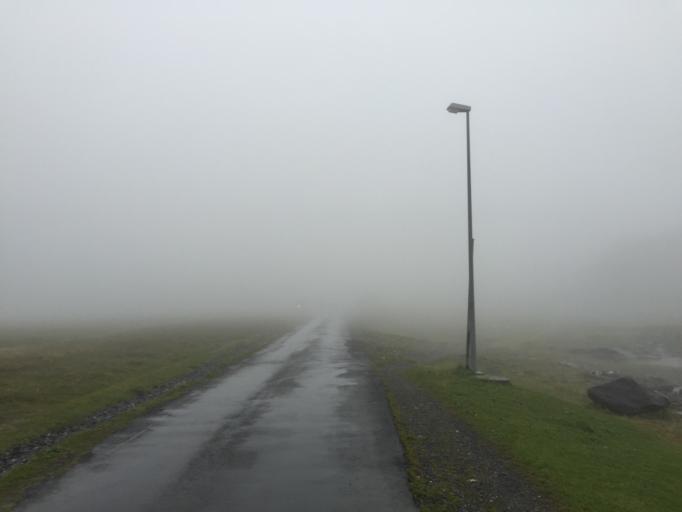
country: CH
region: Bern
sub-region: Interlaken-Oberhasli District
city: Meiringen
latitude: 46.7718
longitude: 8.2784
